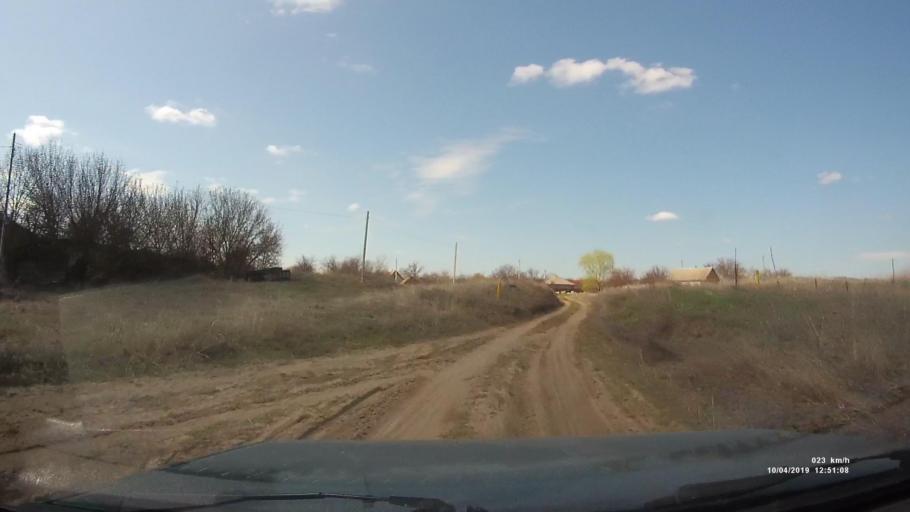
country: RU
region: Rostov
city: Kamensk-Shakhtinskiy
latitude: 48.3588
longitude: 40.2184
